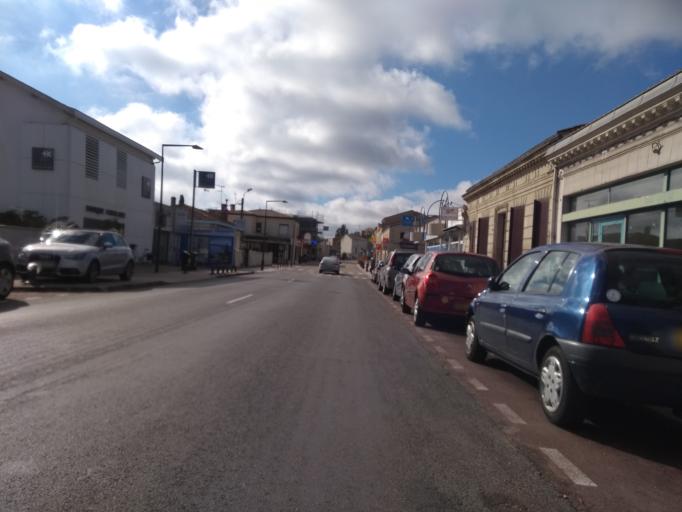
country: FR
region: Aquitaine
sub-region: Departement de la Gironde
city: Gradignan
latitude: 44.7749
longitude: -0.6123
